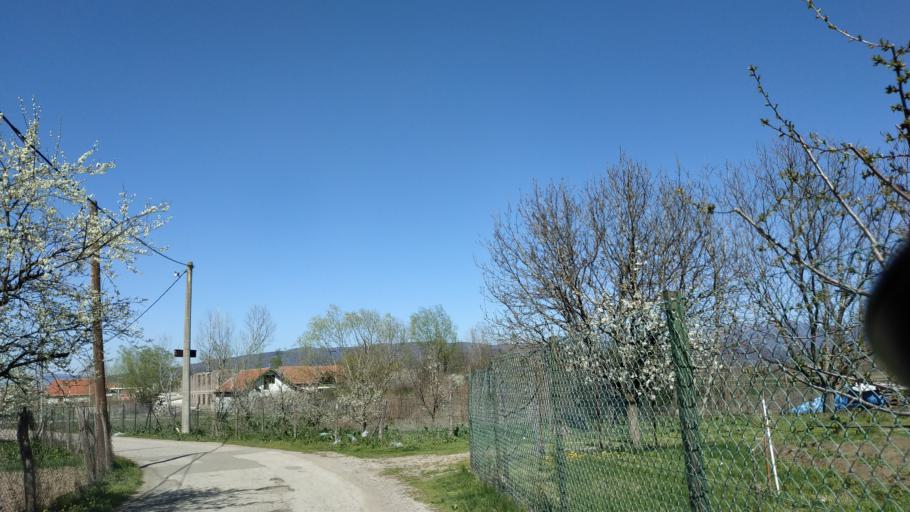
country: RS
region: Central Serbia
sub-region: Nisavski Okrug
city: Aleksinac
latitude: 43.5134
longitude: 21.6988
